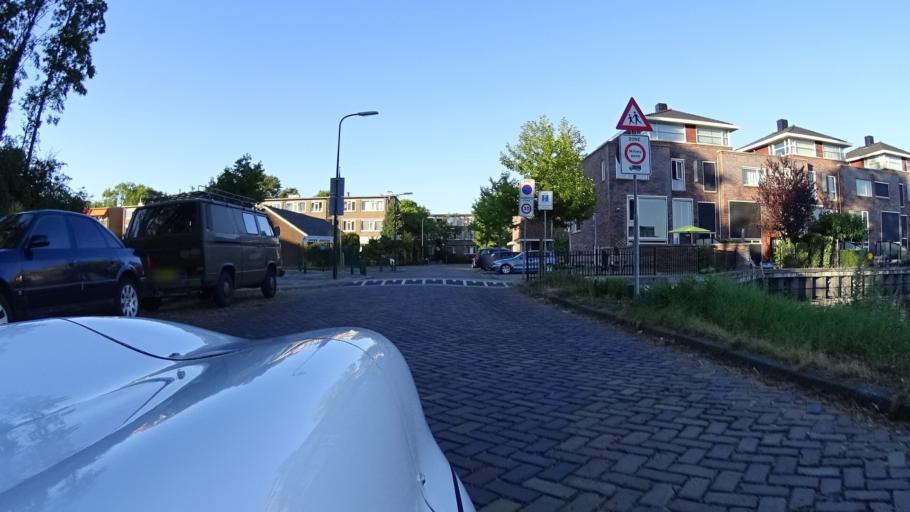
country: NL
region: South Holland
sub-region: Gemeente Rijswijk
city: Rijswijk
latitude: 52.0469
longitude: 4.3396
